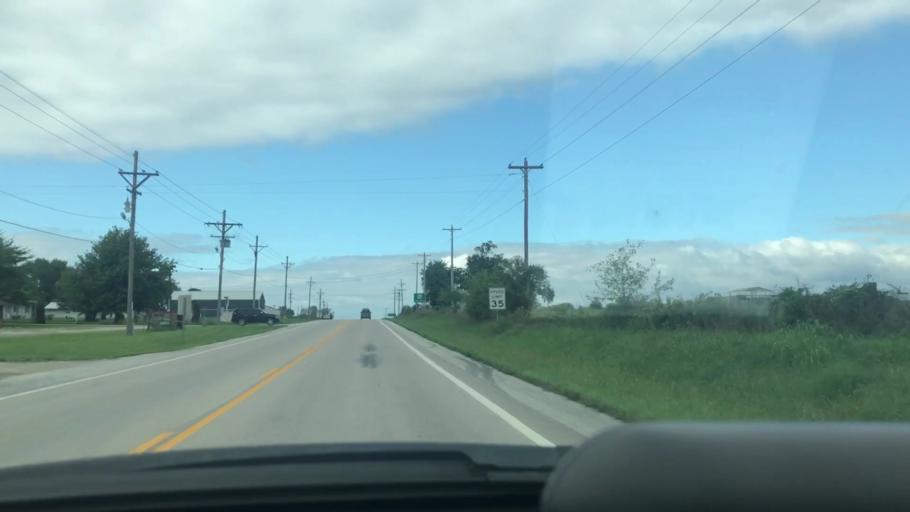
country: US
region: Missouri
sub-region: Hickory County
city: Hermitage
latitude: 37.9372
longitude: -93.2083
